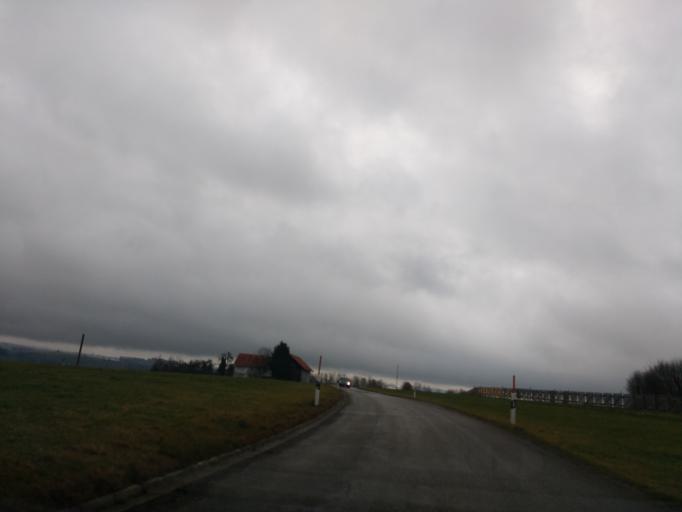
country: DE
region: Bavaria
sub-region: Swabia
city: Neuburg
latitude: 47.7469
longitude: 10.3504
